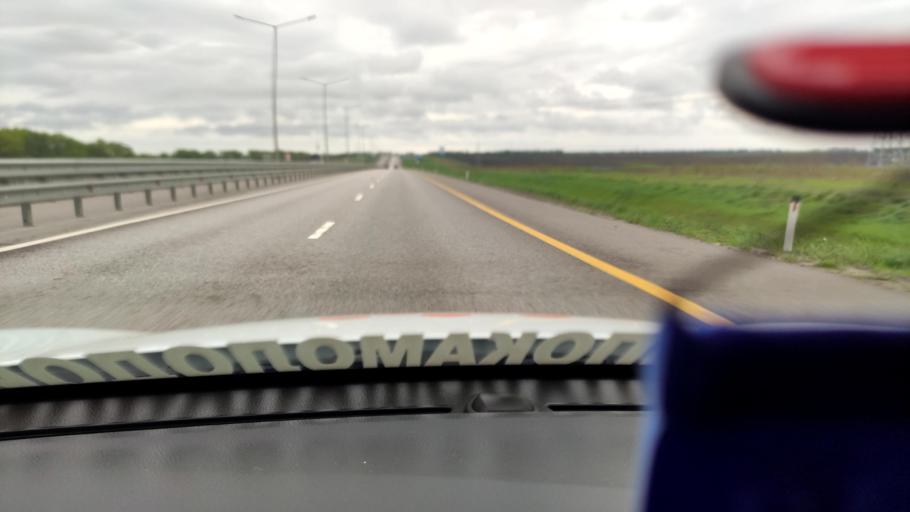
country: RU
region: Voronezj
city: Podkletnoye
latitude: 51.5507
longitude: 39.4912
